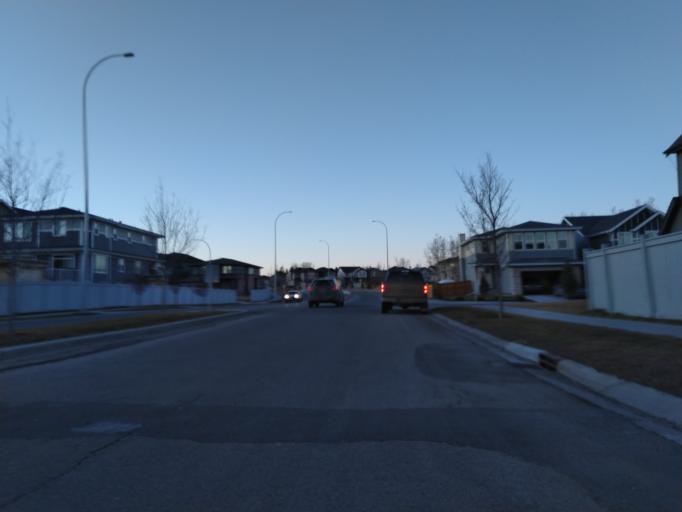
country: CA
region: Alberta
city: Calgary
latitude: 51.1310
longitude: -114.2517
